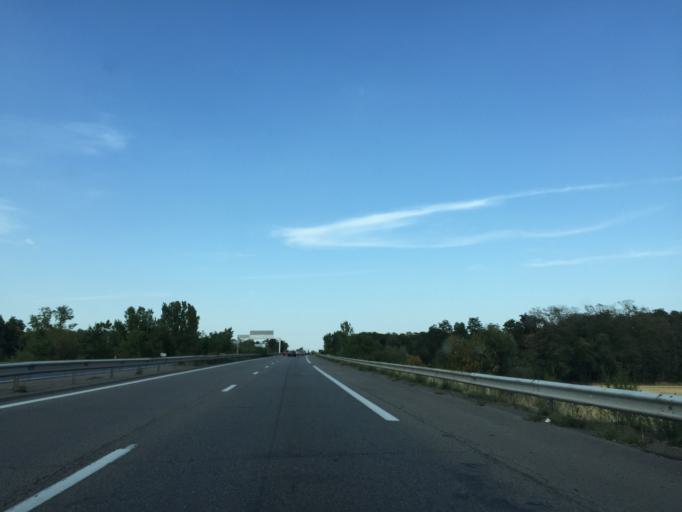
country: FR
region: Alsace
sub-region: Departement du Bas-Rhin
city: Scherwiller
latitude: 48.2743
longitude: 7.4334
